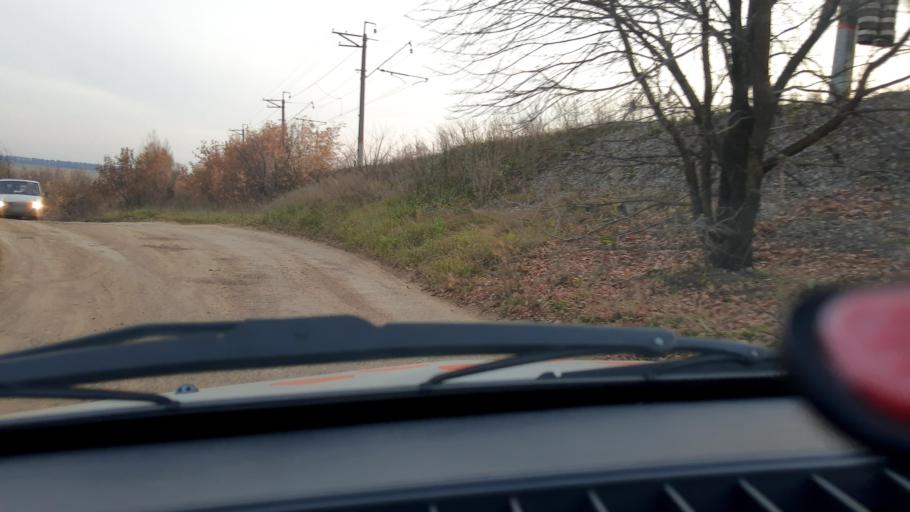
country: RU
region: Bashkortostan
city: Iglino
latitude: 54.7944
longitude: 56.3340
